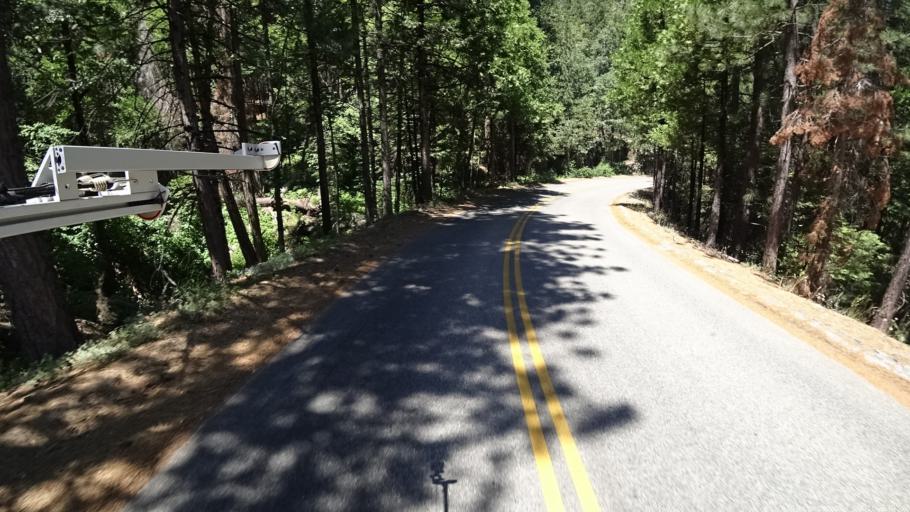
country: US
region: California
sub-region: Madera County
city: Oakhurst
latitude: 37.3581
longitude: -119.3906
